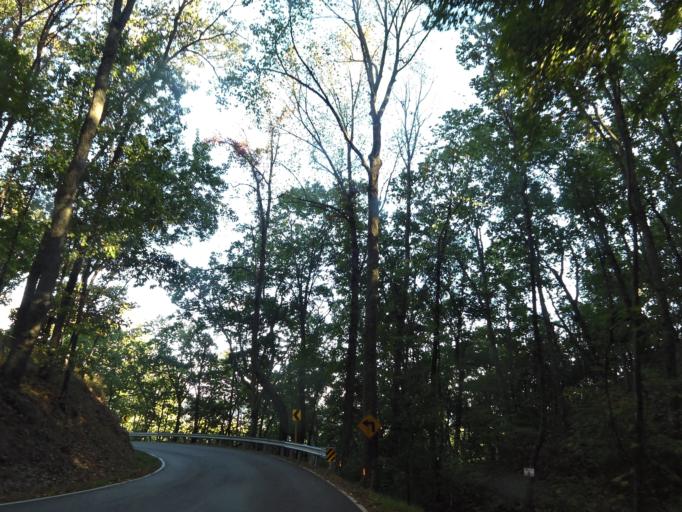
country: US
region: Tennessee
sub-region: Grainger County
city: Blaine
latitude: 36.2376
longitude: -83.6462
